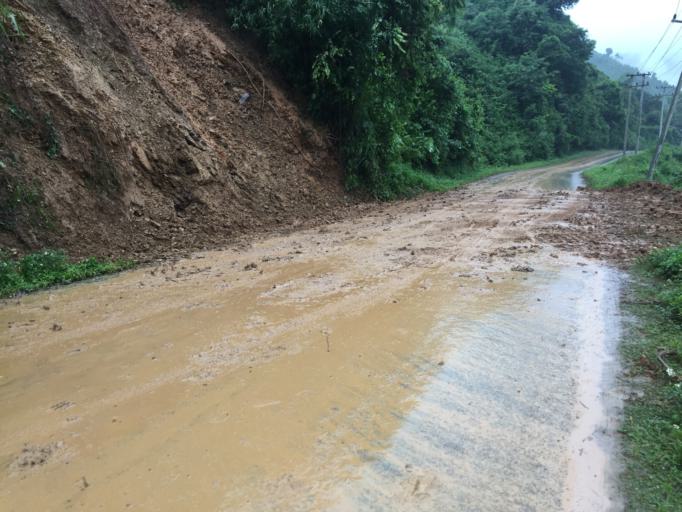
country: TH
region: Nan
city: Chaloem Phra Kiat
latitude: 19.9503
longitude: 101.1967
